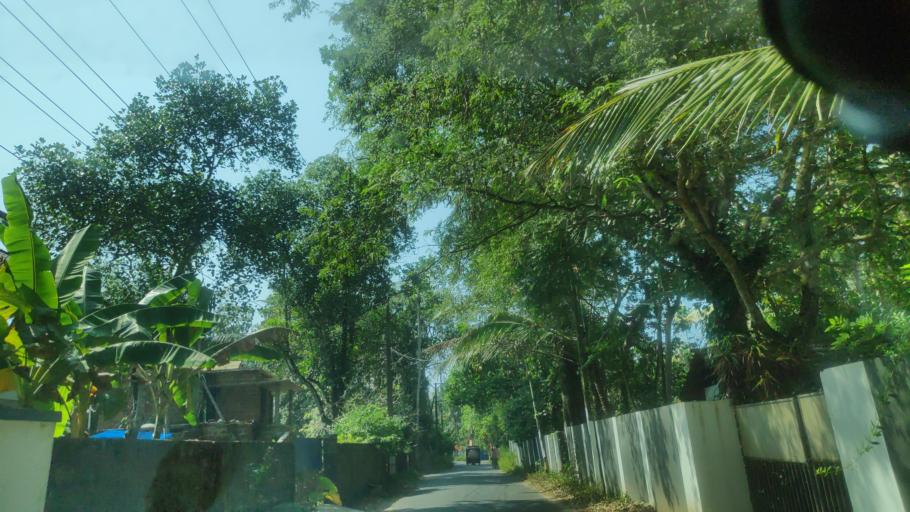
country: IN
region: Kerala
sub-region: Alappuzha
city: Vayalar
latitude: 9.6634
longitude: 76.3104
